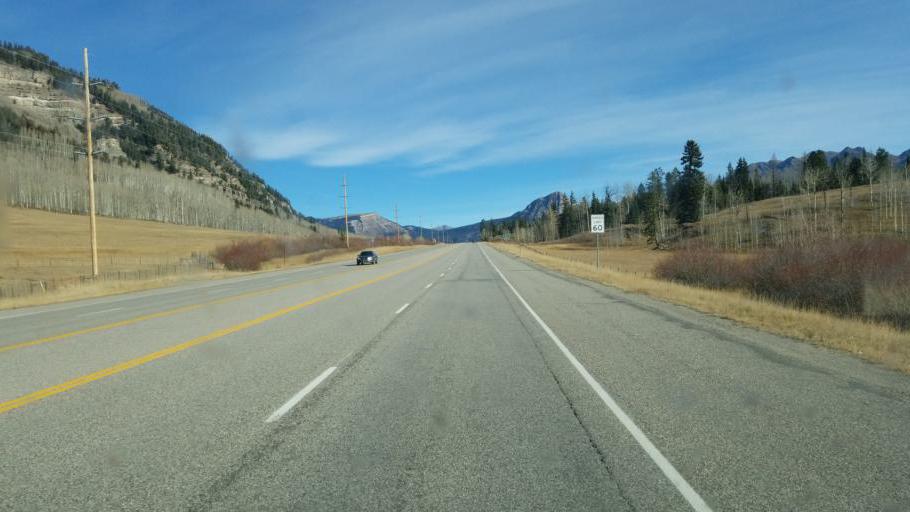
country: US
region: Colorado
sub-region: San Juan County
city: Silverton
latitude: 37.5967
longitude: -107.8214
